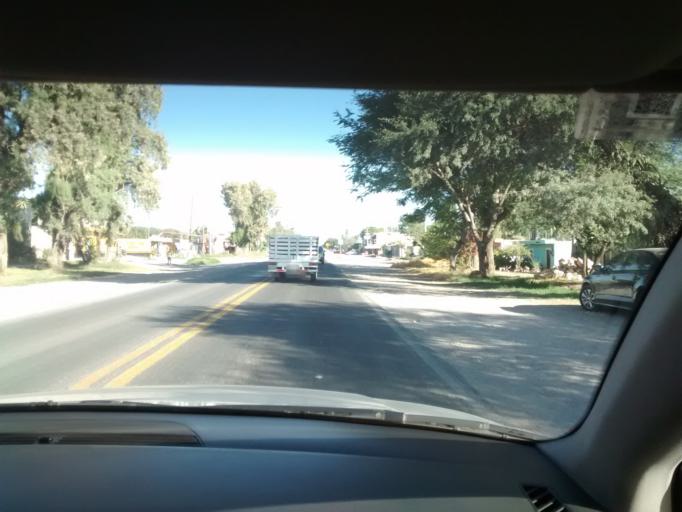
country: MX
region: Puebla
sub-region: Tehuacan
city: Magdalena Cuayucatepec
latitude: 18.5080
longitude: -97.4878
